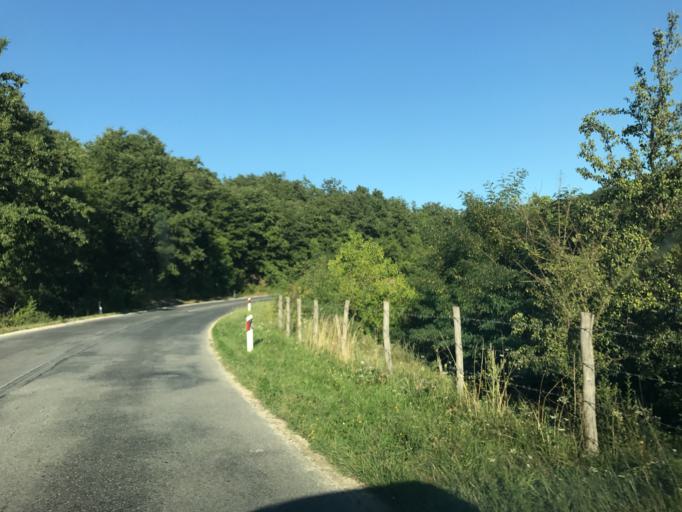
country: RO
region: Mehedinti
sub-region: Comuna Gogosu
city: Ostrovu Mare
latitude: 44.2892
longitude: 22.3276
